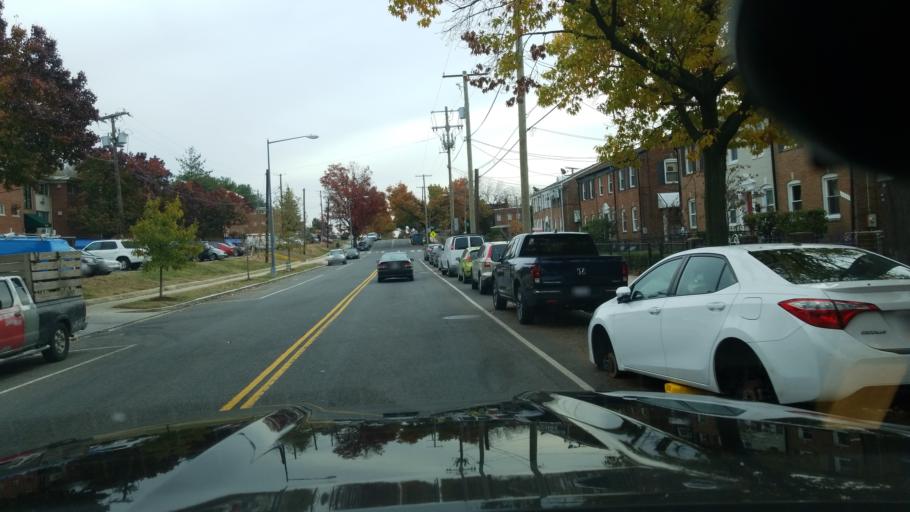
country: US
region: Maryland
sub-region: Prince George's County
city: Chillum
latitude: 38.9636
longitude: -76.9999
